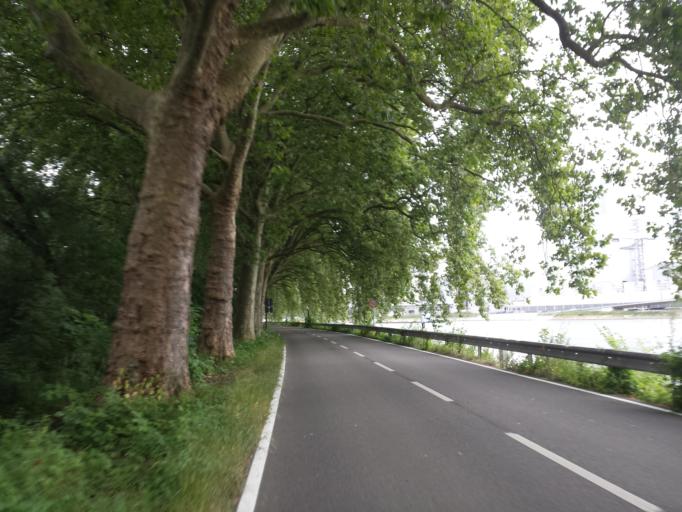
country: DE
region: Rheinland-Pfalz
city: Altrip
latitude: 49.4375
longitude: 8.5050
